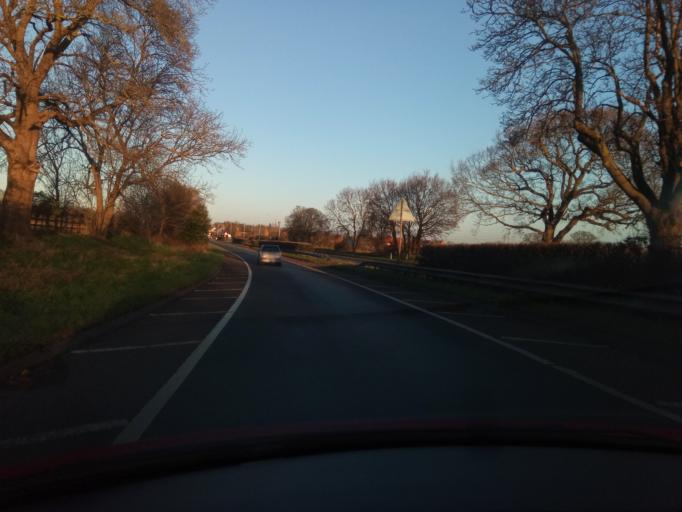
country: GB
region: England
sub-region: Leicestershire
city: Hathern
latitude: 52.7880
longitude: -1.2492
